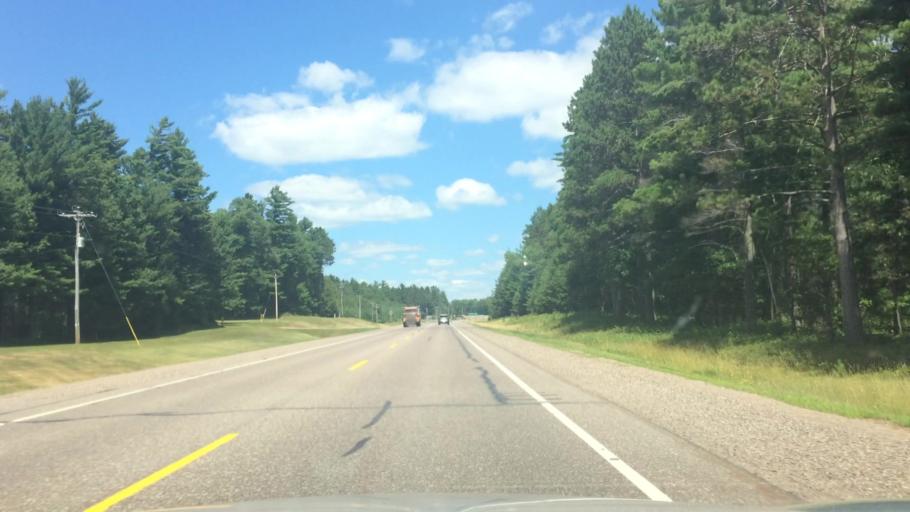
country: US
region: Wisconsin
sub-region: Vilas County
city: Lac du Flambeau
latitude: 45.9333
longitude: -89.6963
